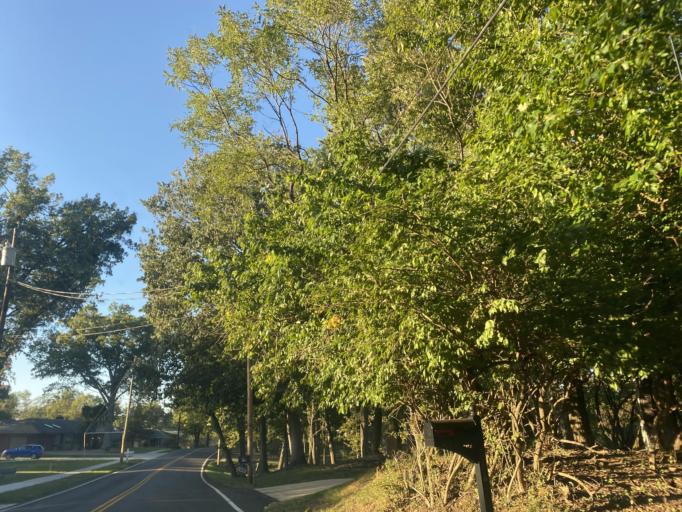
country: US
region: Kentucky
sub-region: Campbell County
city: Dayton
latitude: 39.1031
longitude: -84.4509
